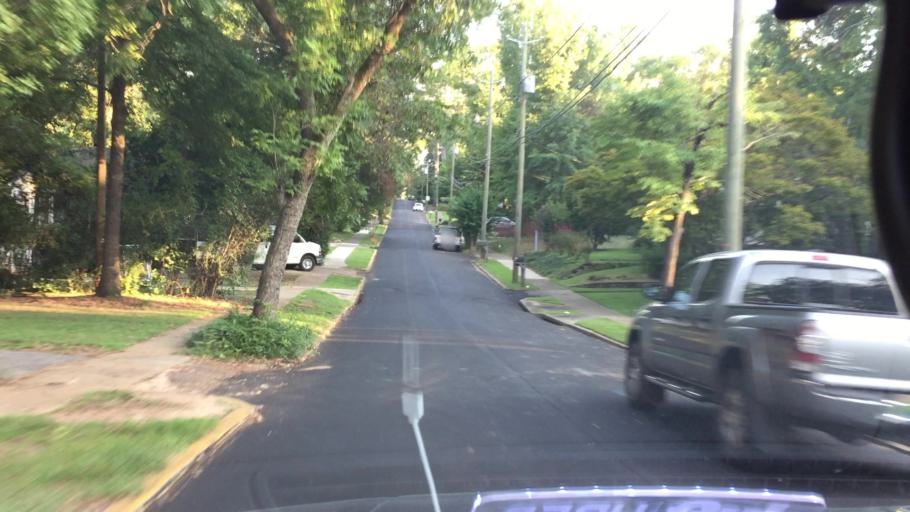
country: US
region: Alabama
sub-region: Lee County
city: Auburn
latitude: 32.6030
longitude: -85.4763
